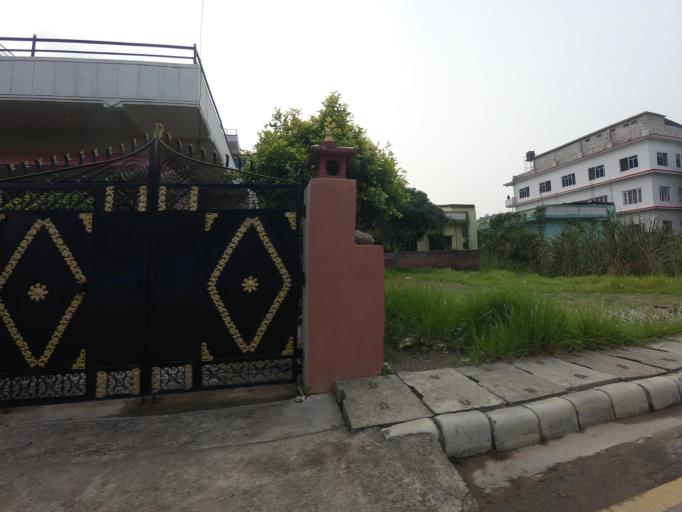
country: NP
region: Western Region
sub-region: Lumbini Zone
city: Bhairahawa
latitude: 27.5202
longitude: 83.4453
